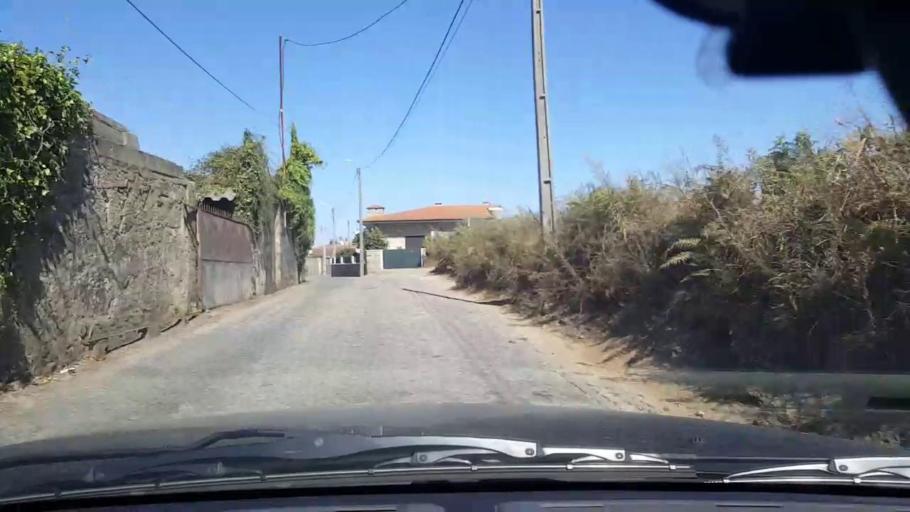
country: PT
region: Porto
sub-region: Maia
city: Gemunde
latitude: 41.2851
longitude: -8.6731
